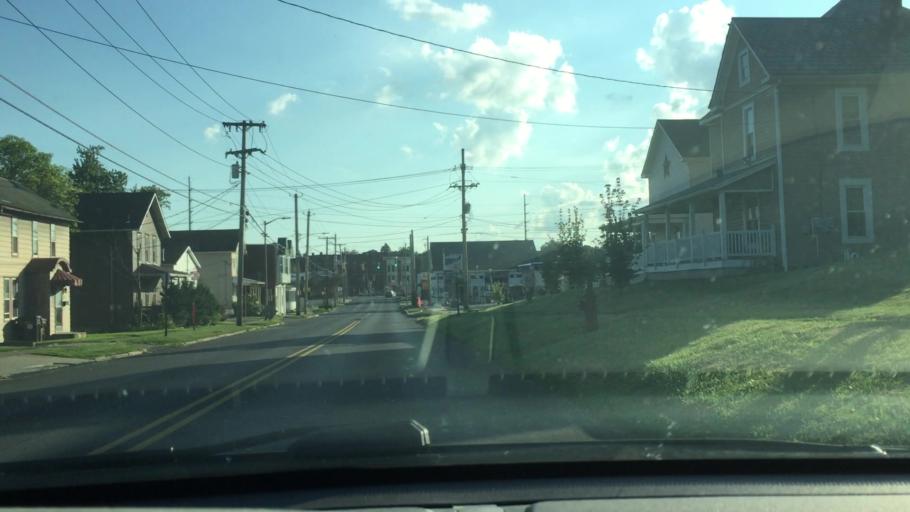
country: US
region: Pennsylvania
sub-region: Mercer County
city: Grove City
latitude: 41.1632
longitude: -80.0845
